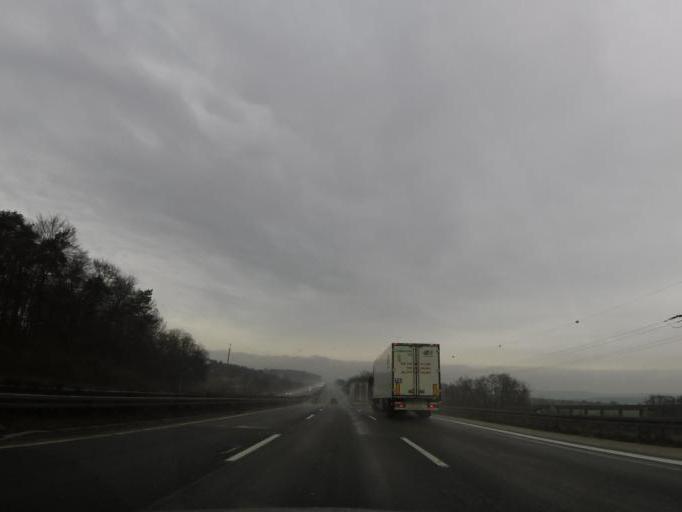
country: DE
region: Hesse
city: Bad Camberg
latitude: 50.2931
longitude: 8.2398
